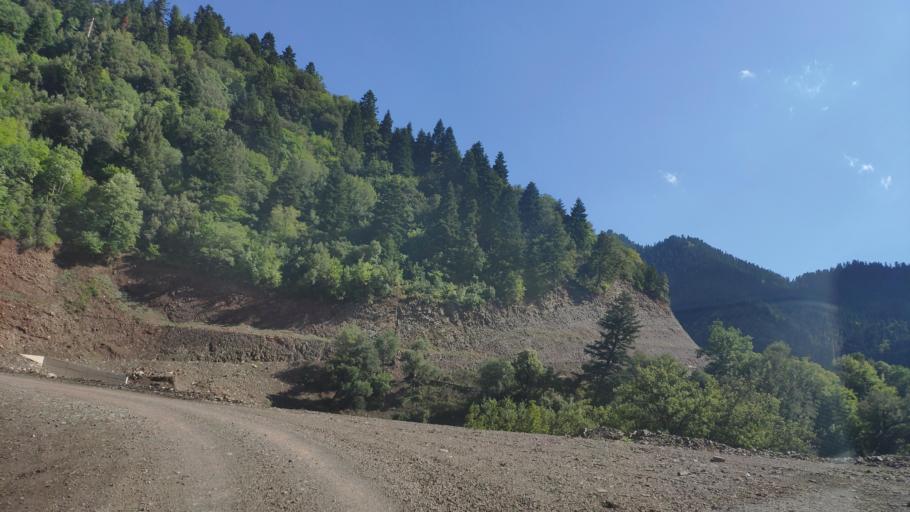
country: GR
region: Central Greece
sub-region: Nomos Evrytanias
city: Kerasochori
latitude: 39.1217
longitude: 21.6256
